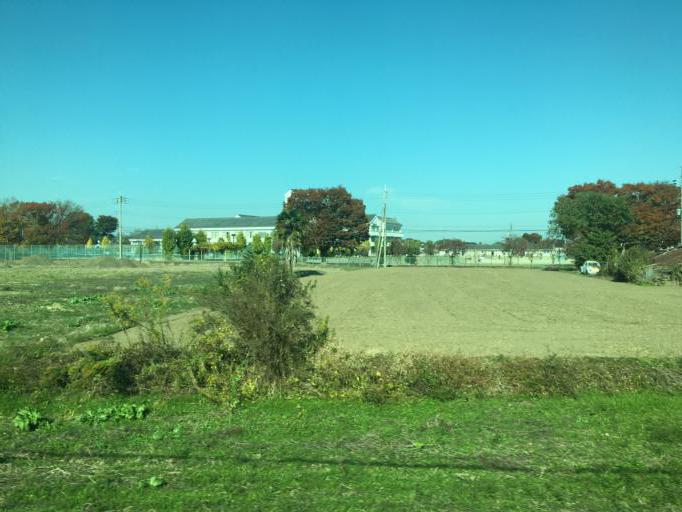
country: JP
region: Ibaraki
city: Yuki
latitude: 36.2970
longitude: 139.8858
